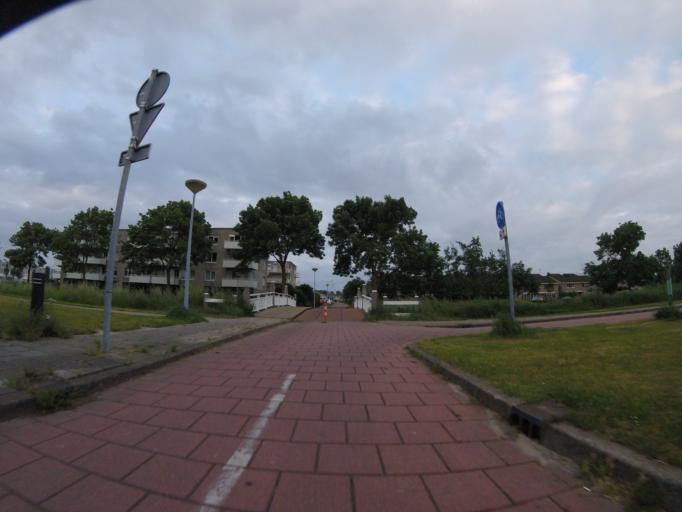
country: NL
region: North Holland
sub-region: Gemeente Haarlemmermeer
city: Hoofddorp
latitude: 52.2997
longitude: 4.6636
